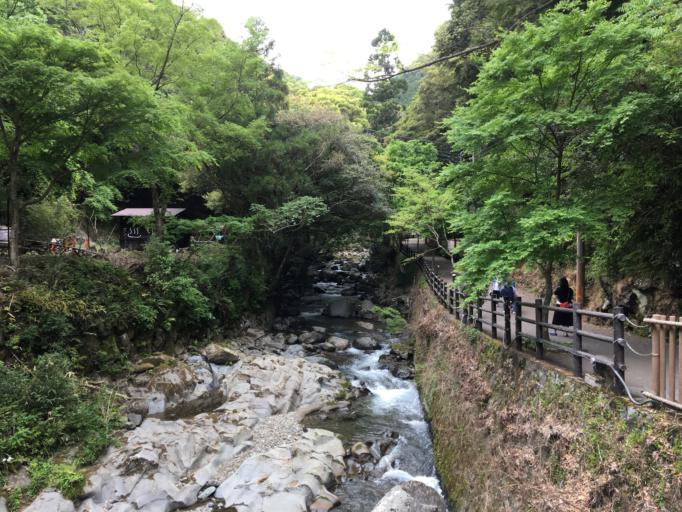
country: JP
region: Shizuoka
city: Shimoda
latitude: 34.7960
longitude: 138.9336
